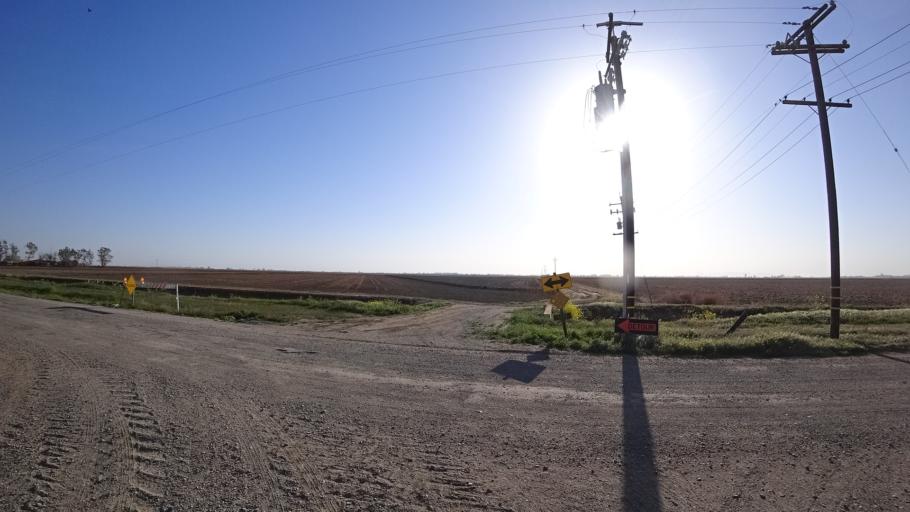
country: US
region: California
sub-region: Colusa County
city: Maxwell
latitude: 39.3852
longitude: -122.2300
